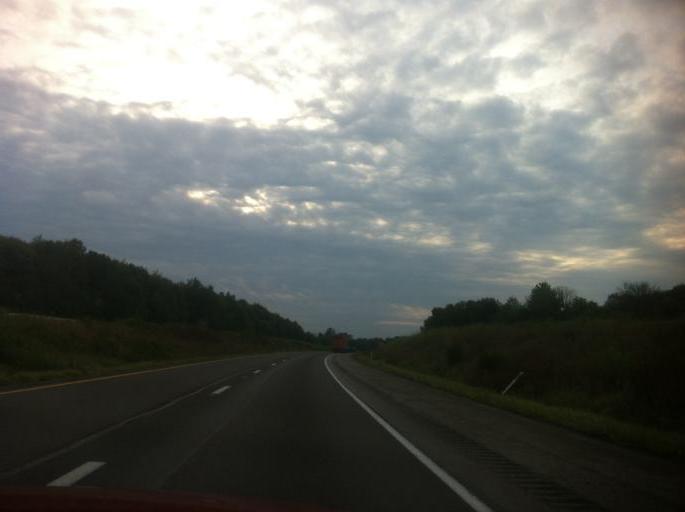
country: US
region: Pennsylvania
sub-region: Venango County
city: Franklin
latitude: 41.1902
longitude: -79.8695
